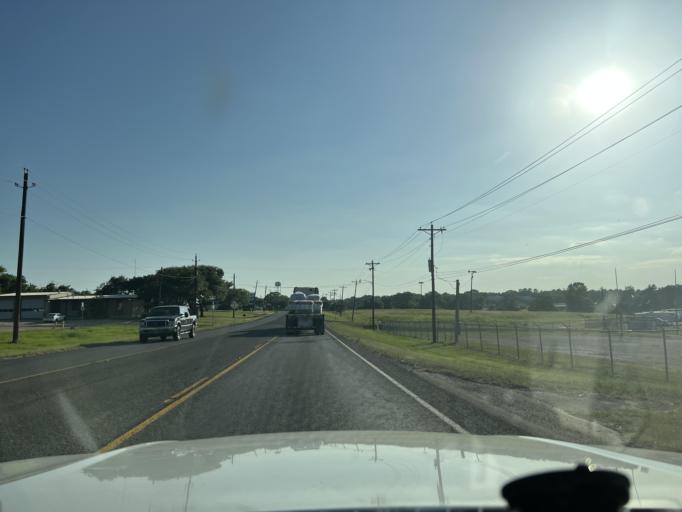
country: US
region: Texas
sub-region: Washington County
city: Brenham
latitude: 30.1787
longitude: -96.3898
